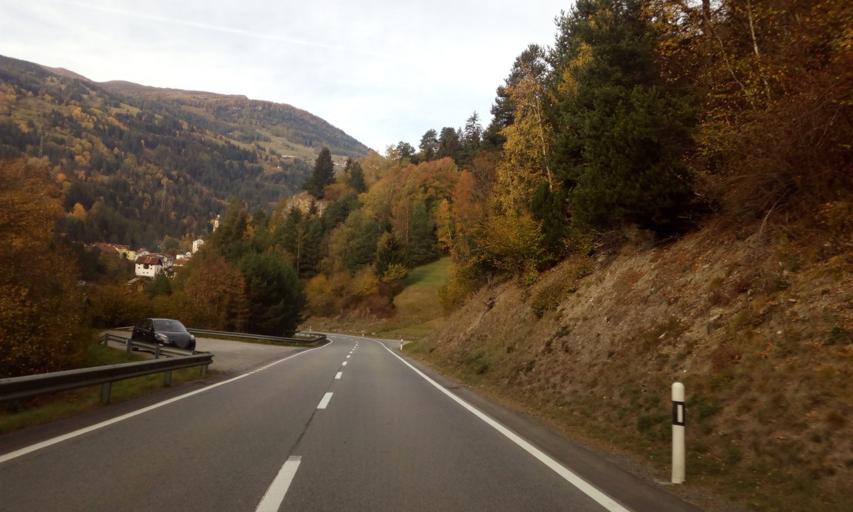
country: CH
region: Grisons
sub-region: Albula District
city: Tiefencastel
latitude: 46.6625
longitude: 9.5838
